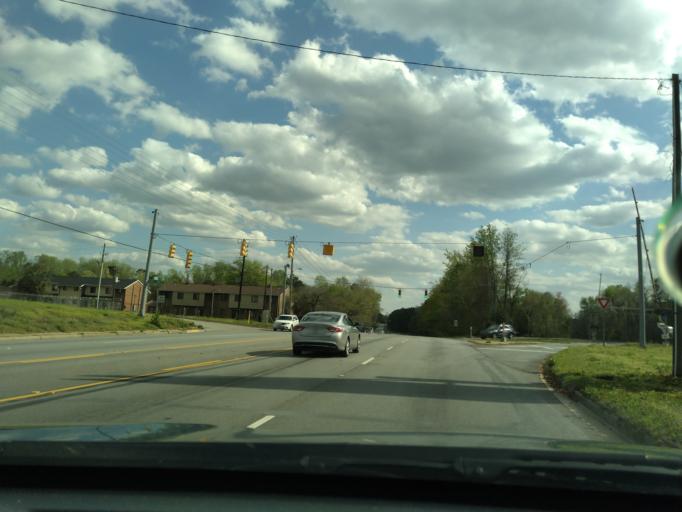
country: US
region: South Carolina
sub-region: Florence County
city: Florence
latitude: 34.1770
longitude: -79.7617
